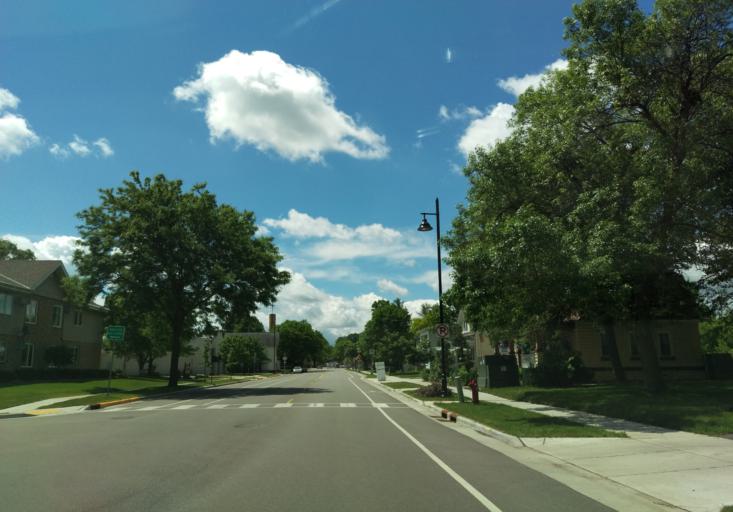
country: US
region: Wisconsin
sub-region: Dane County
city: Middleton
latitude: 43.0992
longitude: -89.5115
